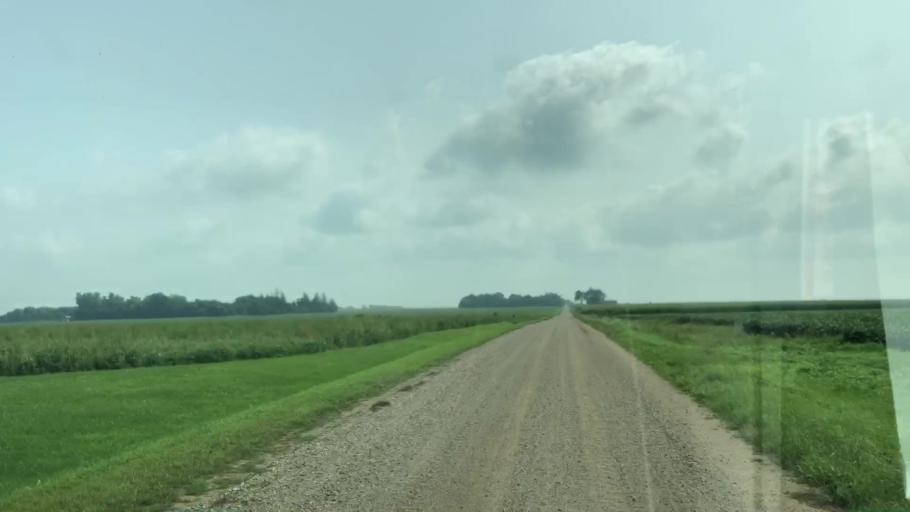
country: US
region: Iowa
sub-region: O'Brien County
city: Sheldon
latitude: 43.2007
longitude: -95.9149
